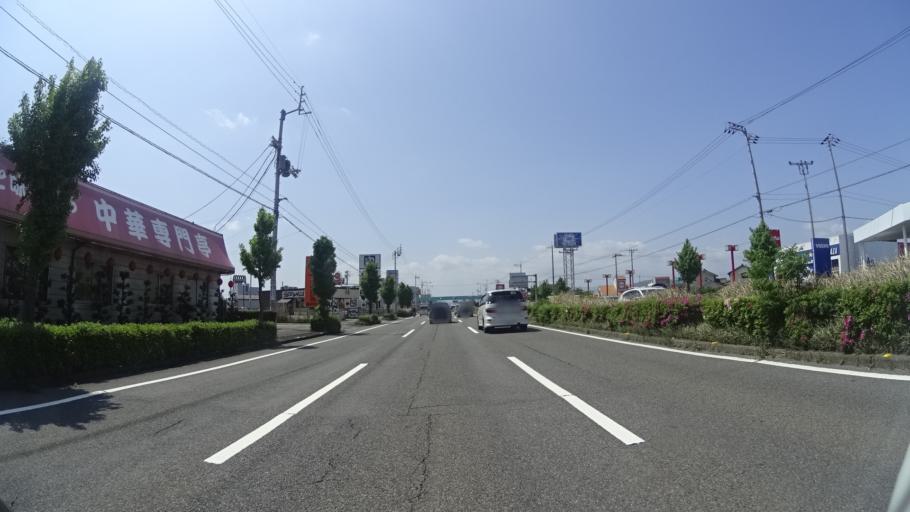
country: JP
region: Tokushima
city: Tokushima-shi
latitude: 34.1141
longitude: 134.5777
